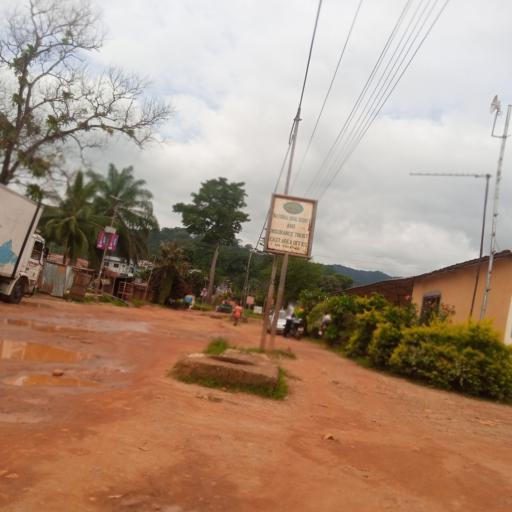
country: SL
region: Eastern Province
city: Kenema
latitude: 7.8770
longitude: -11.1941
